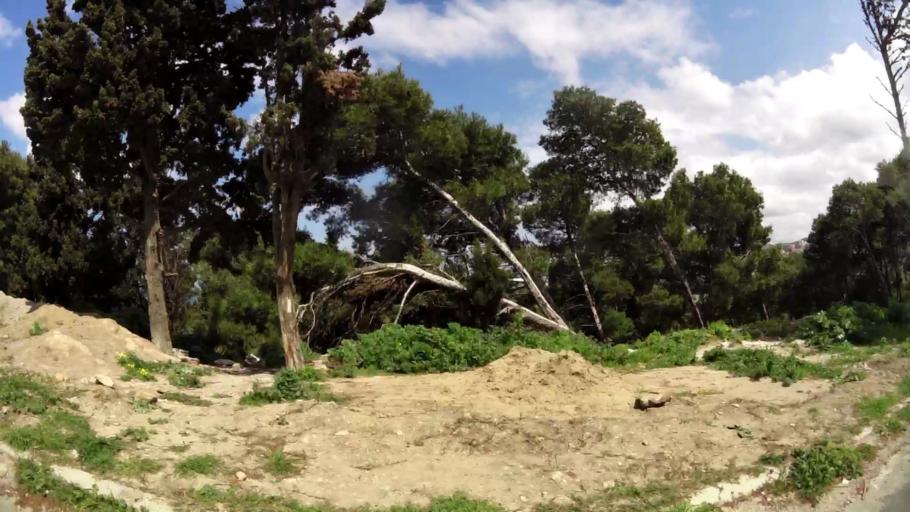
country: MA
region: Tanger-Tetouan
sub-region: Tanger-Assilah
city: Tangier
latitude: 35.7771
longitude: -5.7720
